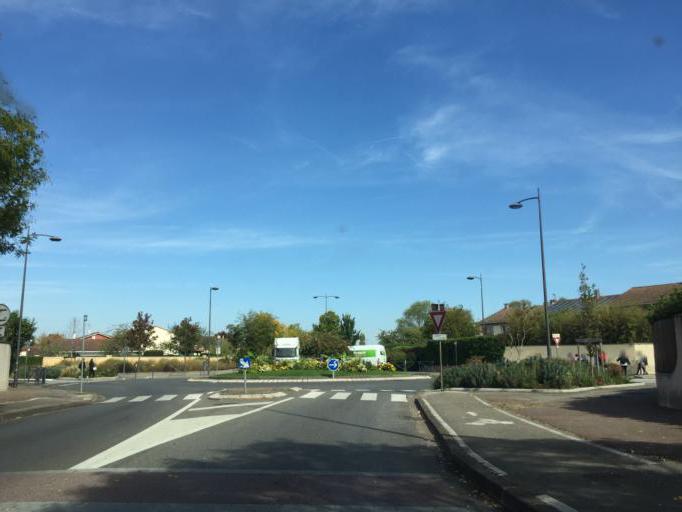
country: FR
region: Rhone-Alpes
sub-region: Departement du Rhone
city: Meyzieu
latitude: 45.7699
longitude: 4.9925
